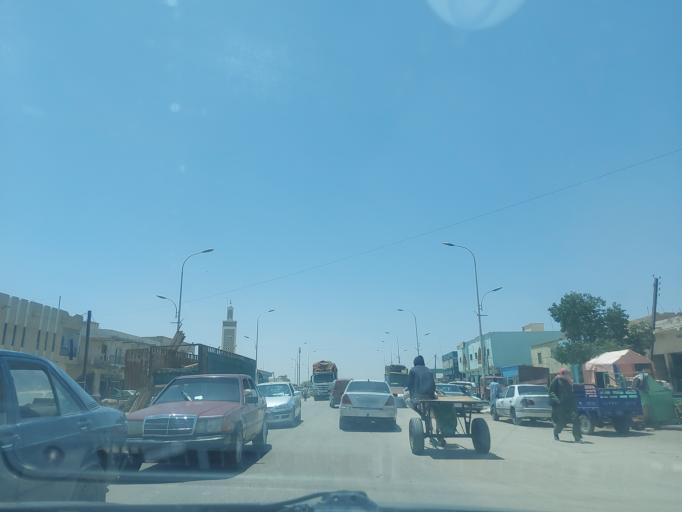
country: MR
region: Nouakchott
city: Nouakchott
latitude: 18.0799
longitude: -15.9818
